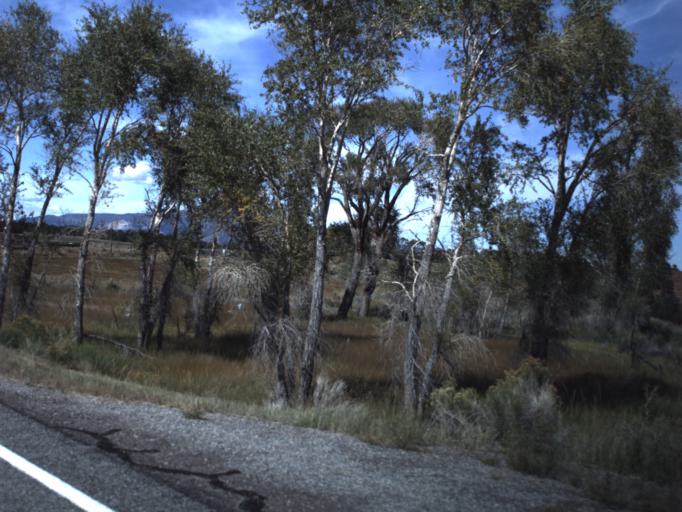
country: US
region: Utah
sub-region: Wayne County
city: Loa
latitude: 38.2277
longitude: -111.3481
